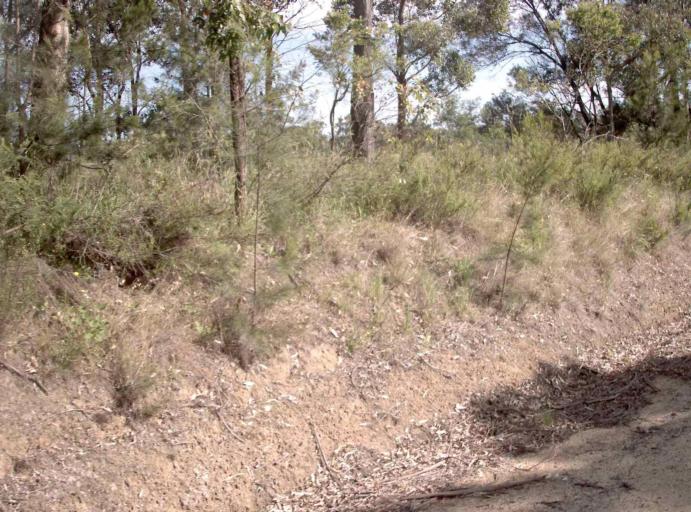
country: AU
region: Victoria
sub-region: East Gippsland
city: Lakes Entrance
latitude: -37.5296
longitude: 148.1544
